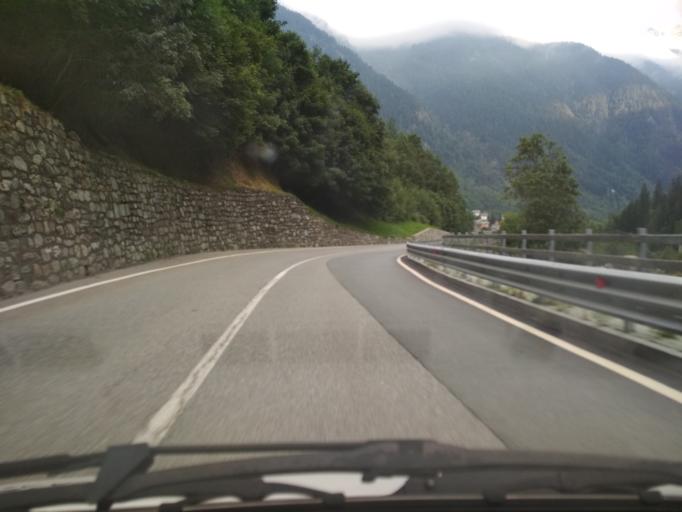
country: IT
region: Aosta Valley
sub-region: Valle d'Aosta
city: Gaby
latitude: 45.7210
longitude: 7.8758
